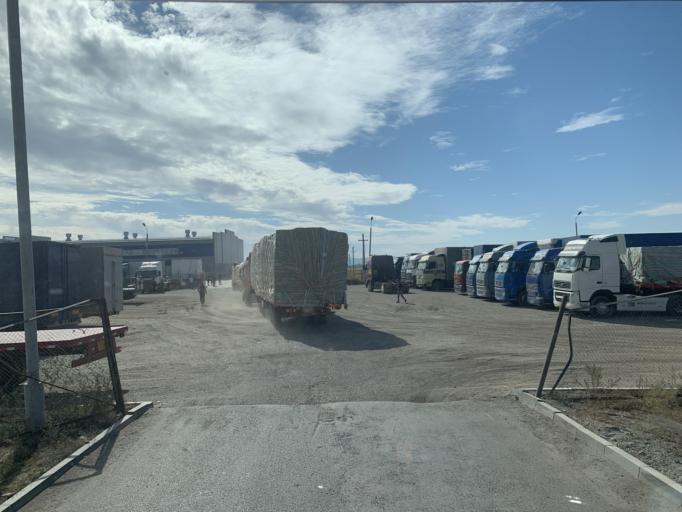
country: CN
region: Xinjiang Uygur Zizhiqu
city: Tacheng
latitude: 46.6792
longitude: 82.7747
